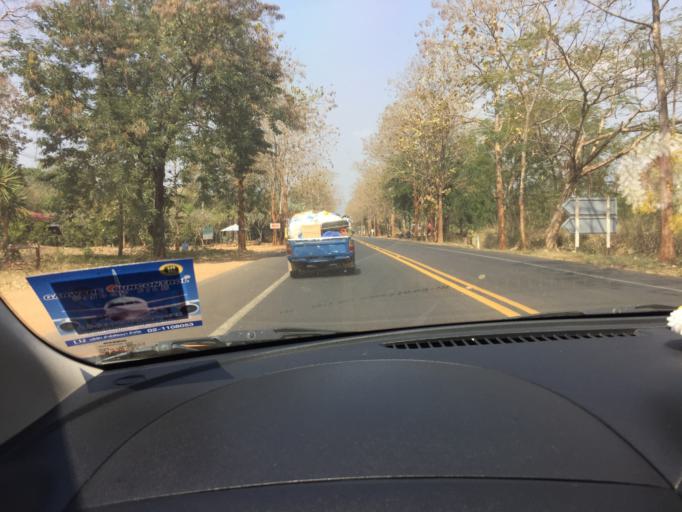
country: TH
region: Kanchanaburi
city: Sai Yok
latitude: 14.1758
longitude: 99.1281
